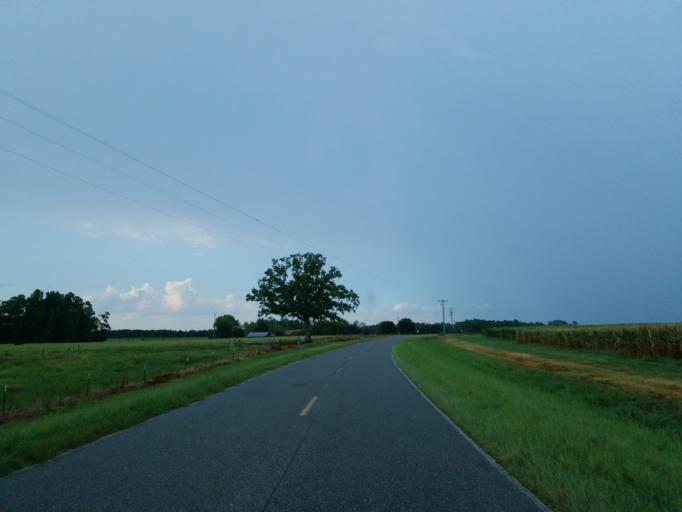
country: US
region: Georgia
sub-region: Cook County
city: Adel
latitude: 31.0820
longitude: -83.4278
